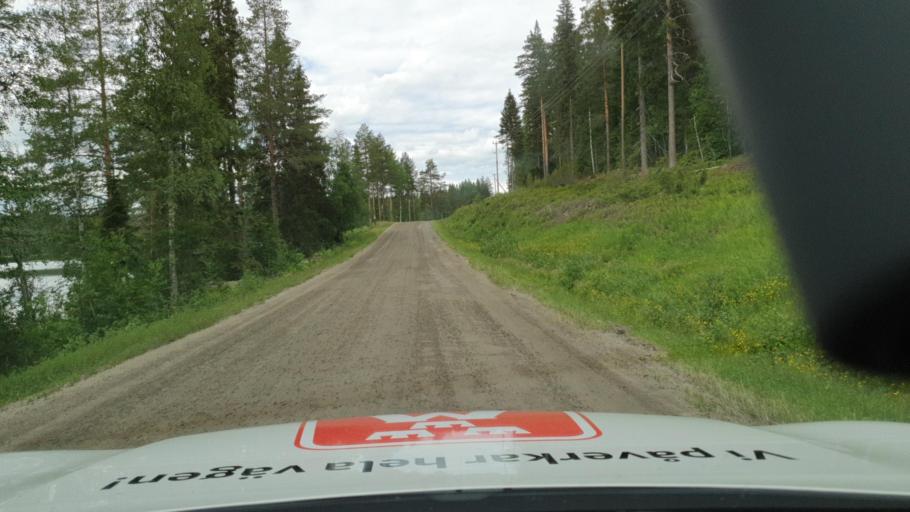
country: SE
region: Vaesterbotten
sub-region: Bjurholms Kommun
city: Bjurholm
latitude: 63.8431
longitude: 18.9906
